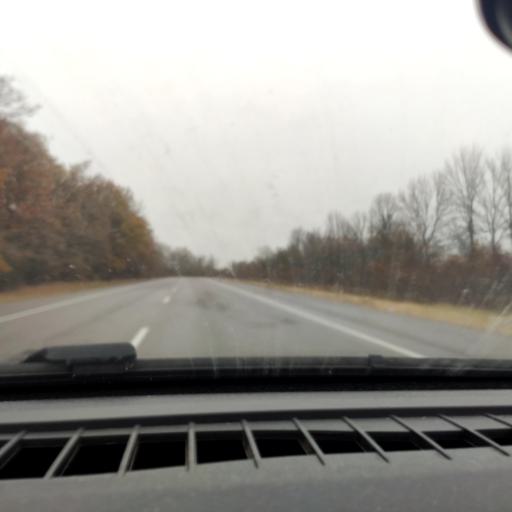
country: RU
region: Voronezj
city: Kolodeznyy
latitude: 51.2852
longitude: 39.0416
